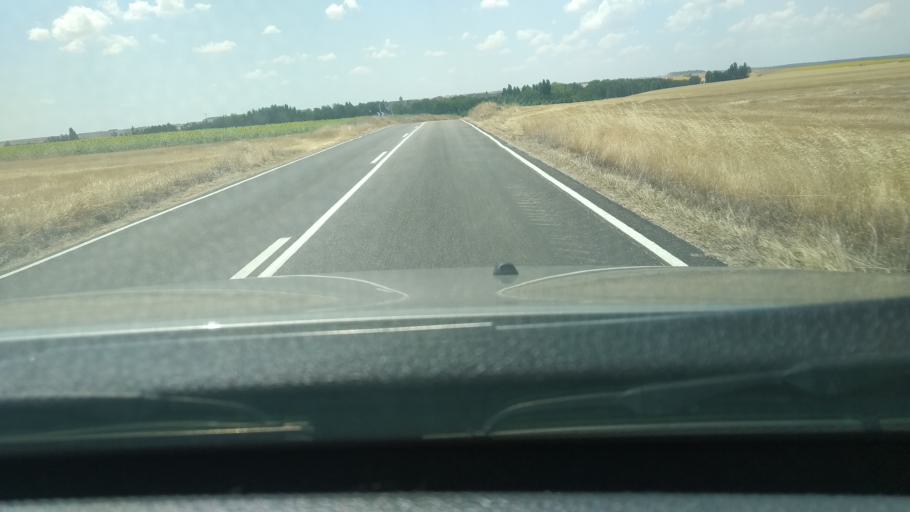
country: ES
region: Castille and Leon
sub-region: Provincia de Burgos
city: Villafruela
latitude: 41.9230
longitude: -3.9015
